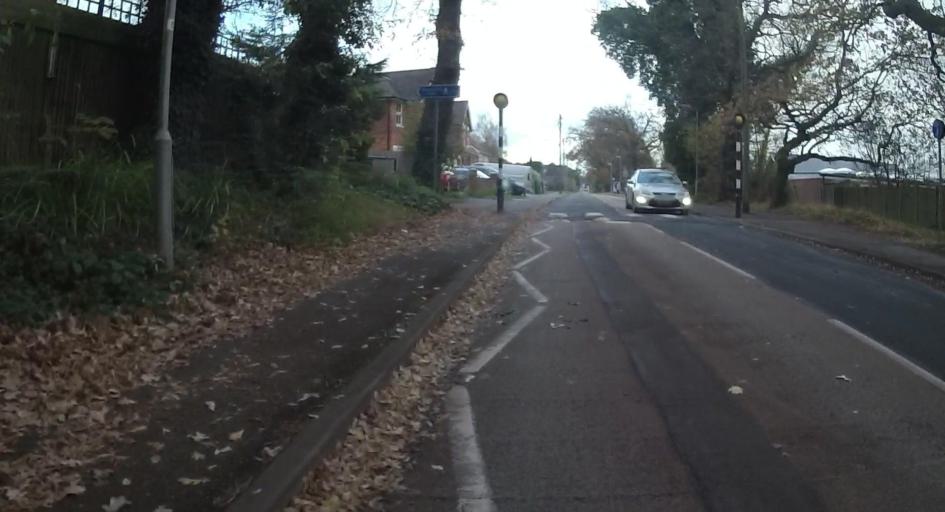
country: GB
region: England
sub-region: Bracknell Forest
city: Sandhurst
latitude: 51.3497
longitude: -0.7827
